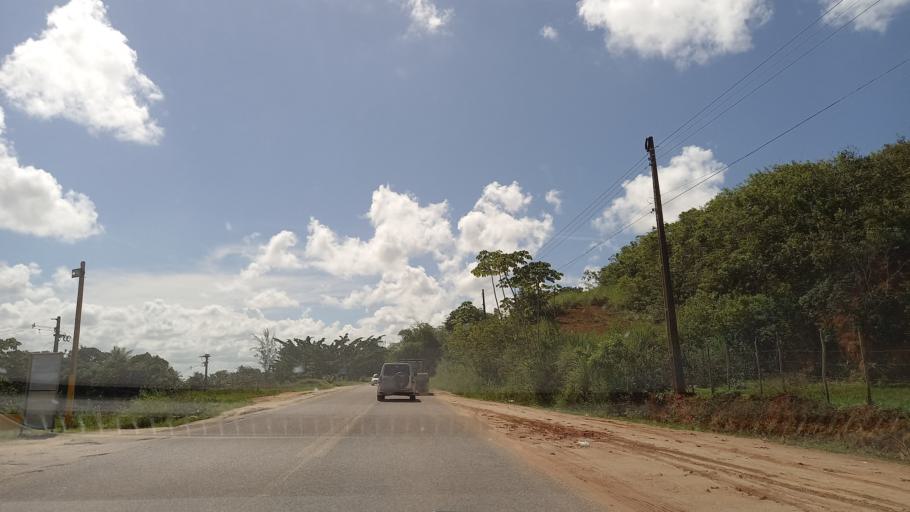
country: BR
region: Pernambuco
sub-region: Barreiros
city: Barreiros
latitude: -8.8035
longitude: -35.1879
